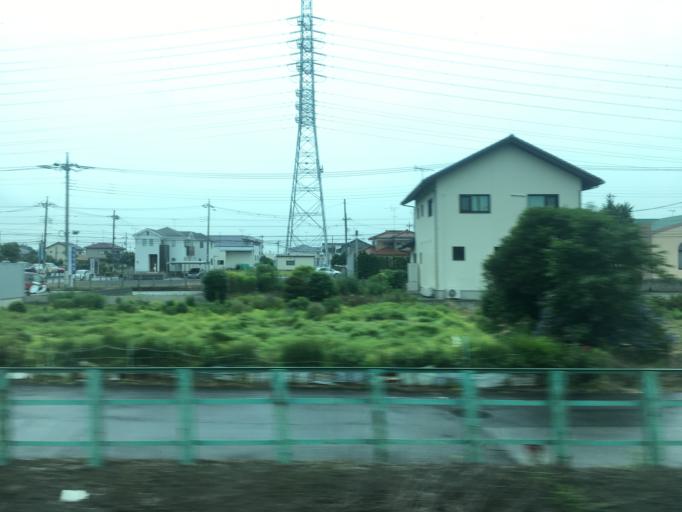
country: JP
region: Tochigi
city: Oyama
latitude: 36.2636
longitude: 139.7661
